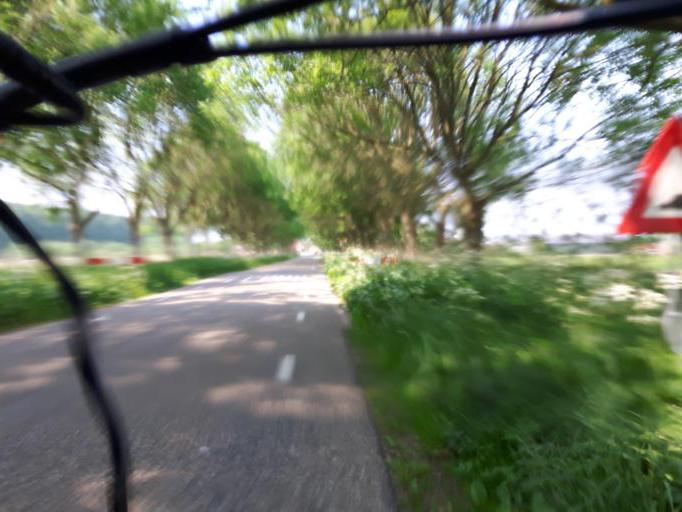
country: NL
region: North Brabant
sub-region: Gemeente Steenbergen
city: Welberg
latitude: 51.5706
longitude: 4.3384
